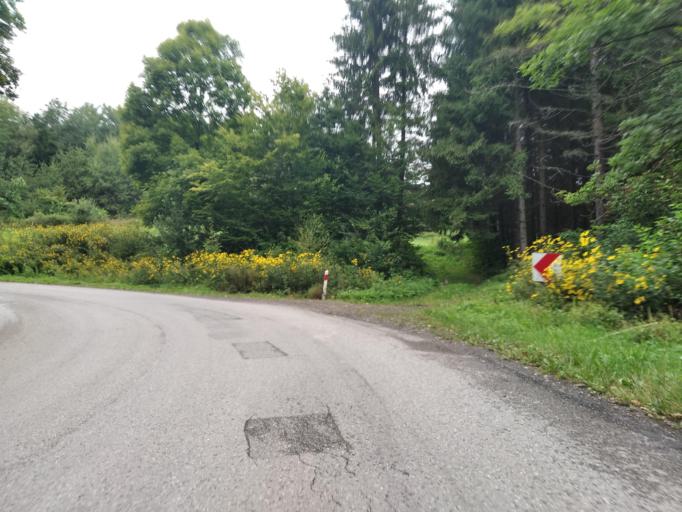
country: PL
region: Subcarpathian Voivodeship
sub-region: Powiat rzeszowski
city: Dynow
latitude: 49.7259
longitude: 22.2981
